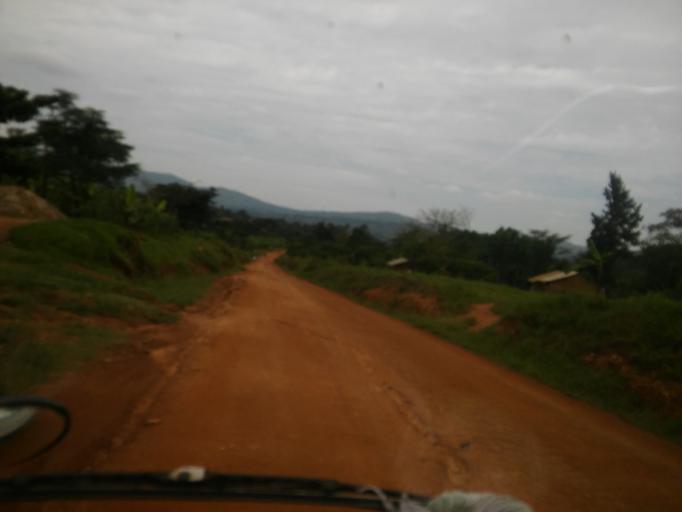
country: UG
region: Eastern Region
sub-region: Mbale District
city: Mbale
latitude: 0.9657
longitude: 34.2099
